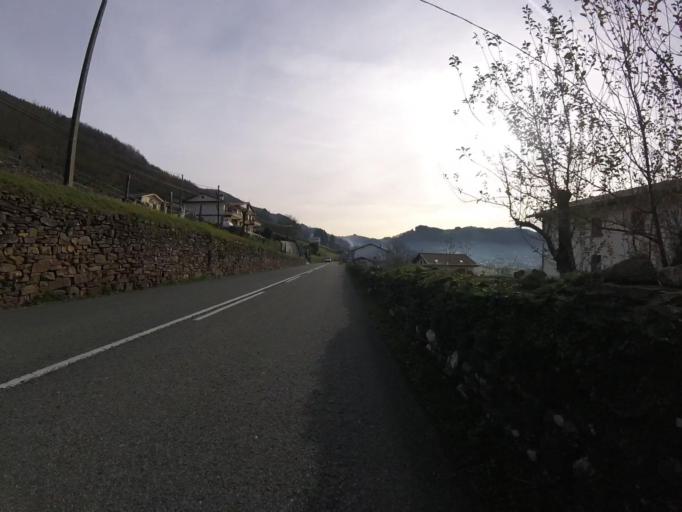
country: ES
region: Basque Country
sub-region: Provincia de Guipuzcoa
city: Berastegui
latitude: 43.1298
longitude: -1.9844
